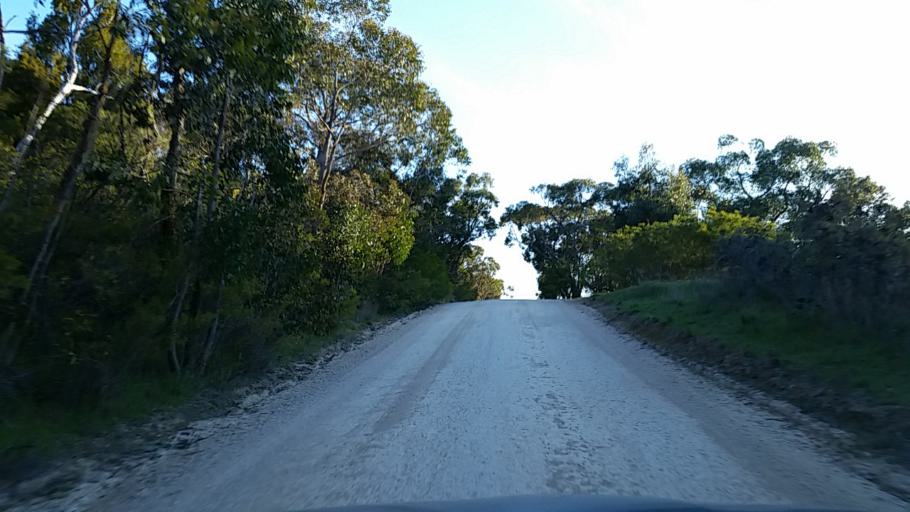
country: AU
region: South Australia
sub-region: Alexandrina
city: Mount Compass
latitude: -35.3042
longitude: 138.6769
